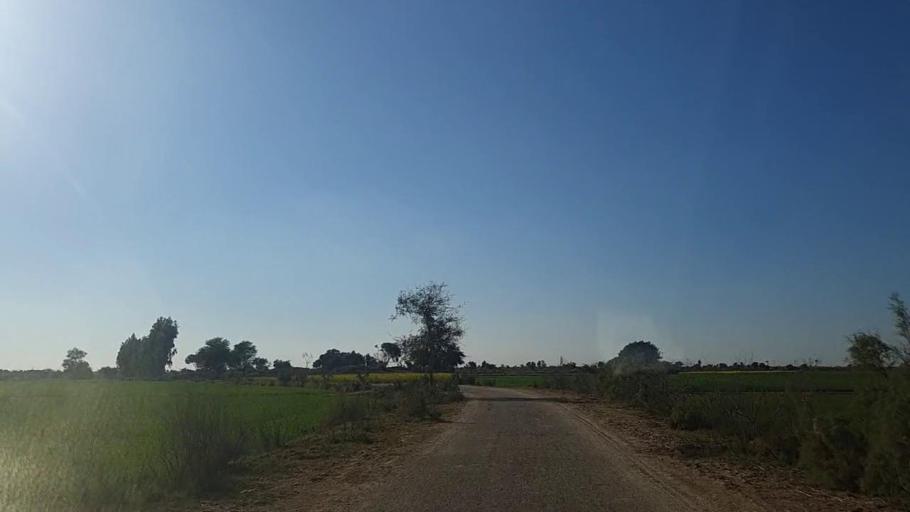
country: PK
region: Sindh
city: Khadro
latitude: 26.2422
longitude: 68.8932
